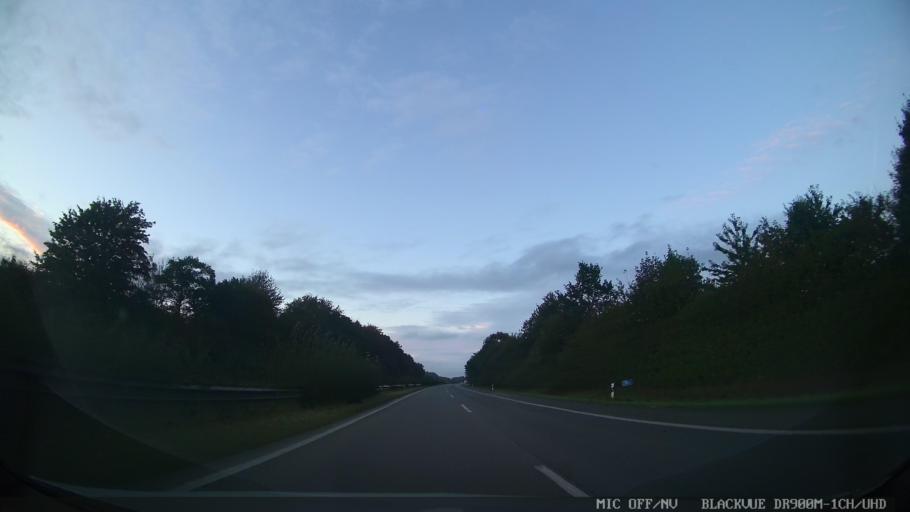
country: DE
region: Schleswig-Holstein
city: Ratekau
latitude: 53.9757
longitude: 10.7327
